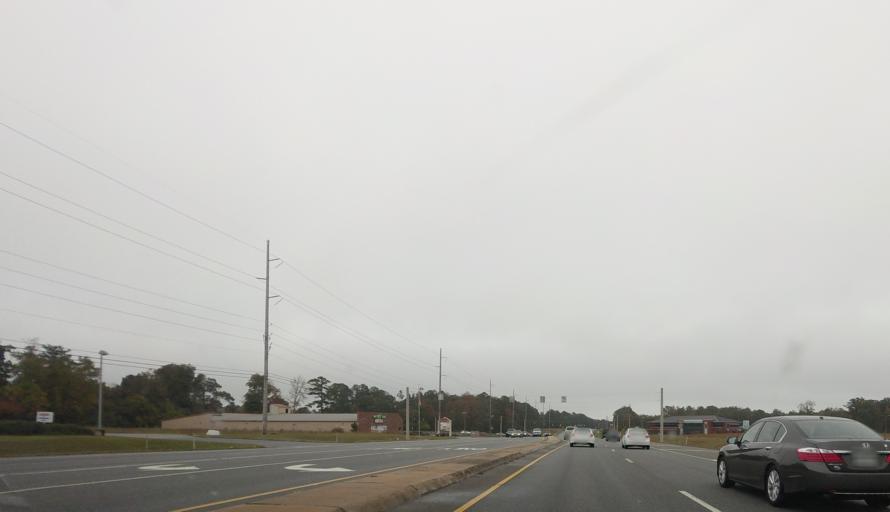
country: US
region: Georgia
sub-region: Houston County
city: Centerville
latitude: 32.5926
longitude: -83.6675
